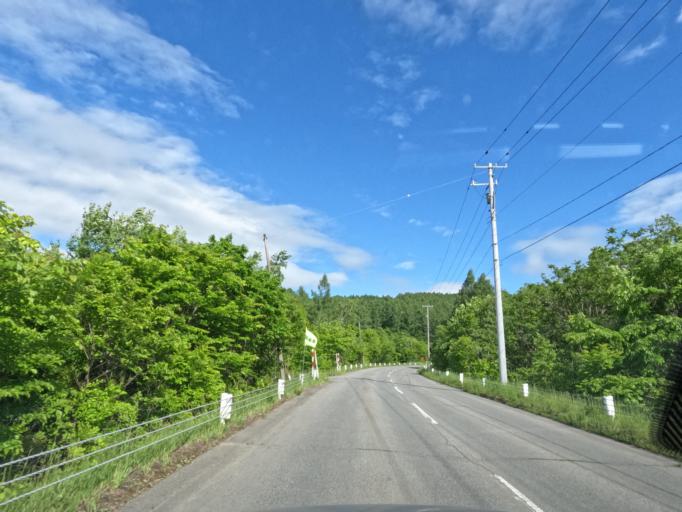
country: JP
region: Hokkaido
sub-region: Asahikawa-shi
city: Asahikawa
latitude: 43.7381
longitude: 142.5363
